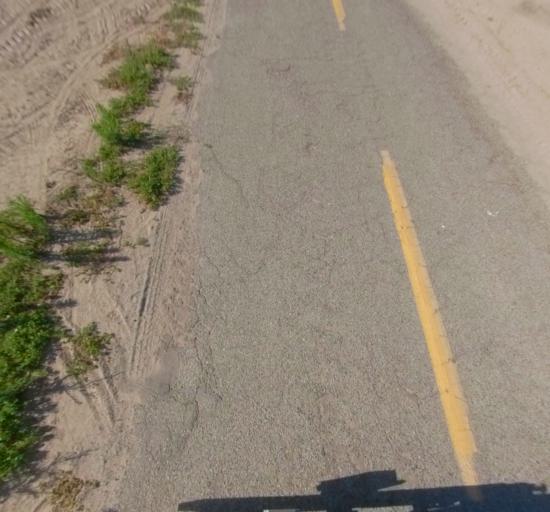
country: US
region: California
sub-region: Fresno County
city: Biola
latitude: 36.8336
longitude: -120.1059
